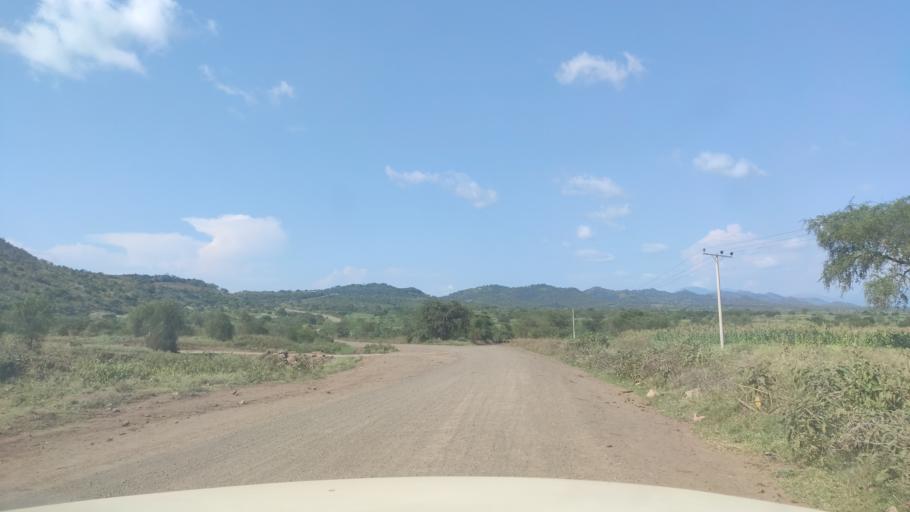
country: ET
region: Southern Nations, Nationalities, and People's Region
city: Felege Neway
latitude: 6.3736
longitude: 37.0869
